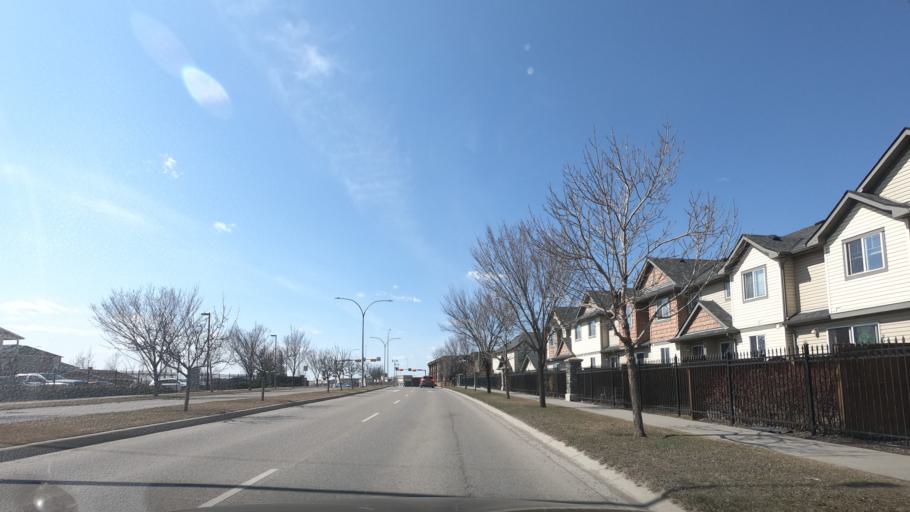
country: CA
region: Alberta
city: Airdrie
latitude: 51.2676
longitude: -113.9889
